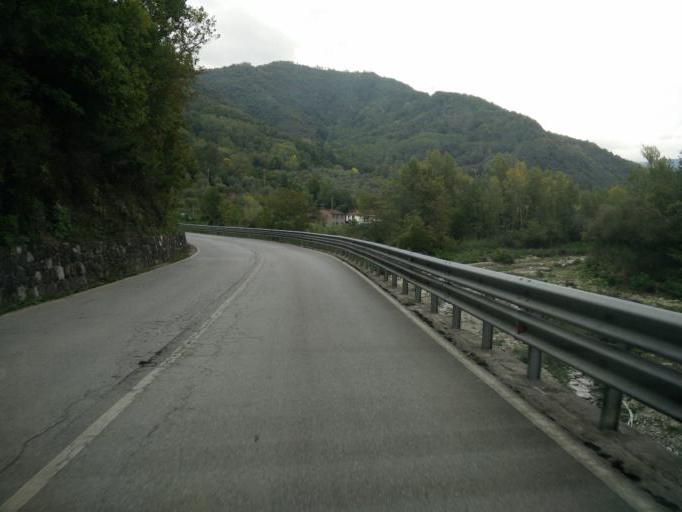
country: IT
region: Tuscany
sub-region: Provincia di Massa-Carrara
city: Casola in Lunigiana
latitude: 44.1948
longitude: 10.1549
